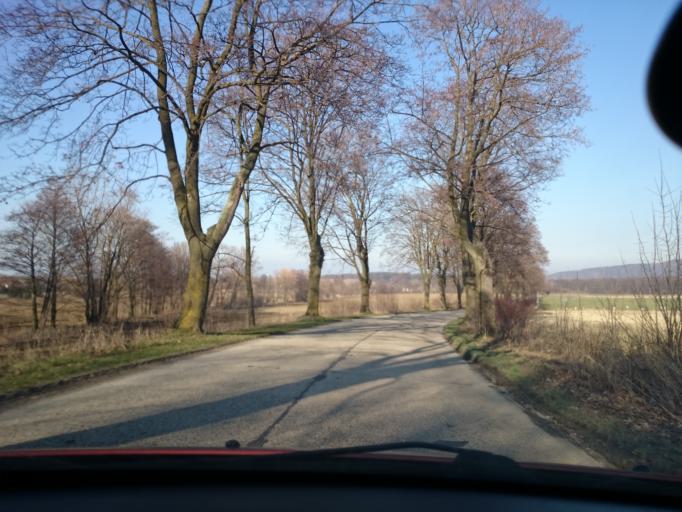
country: PL
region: Lower Silesian Voivodeship
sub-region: Powiat klodzki
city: Bystrzyca Klodzka
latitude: 50.3452
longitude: 16.5930
